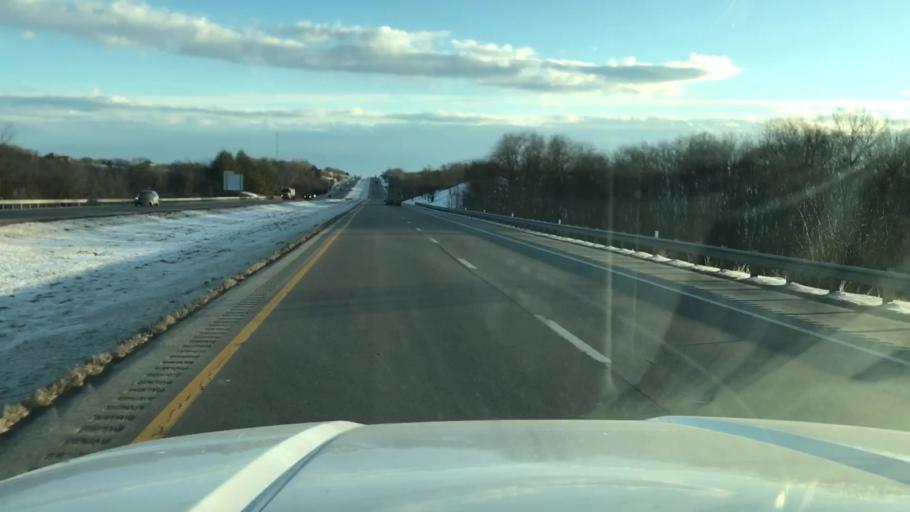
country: US
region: Missouri
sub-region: Andrew County
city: Country Club Village
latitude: 39.8429
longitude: -94.8054
